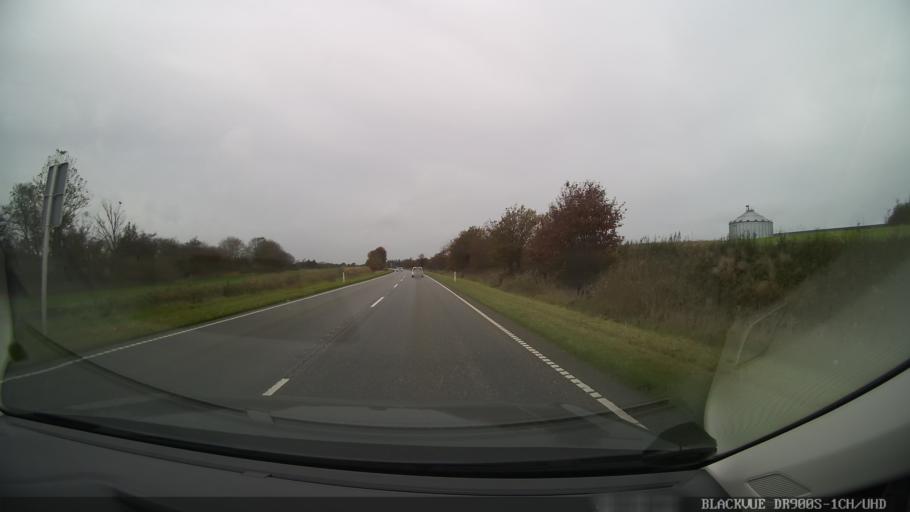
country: DK
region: North Denmark
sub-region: Morso Kommune
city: Nykobing Mors
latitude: 56.8231
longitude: 8.7645
